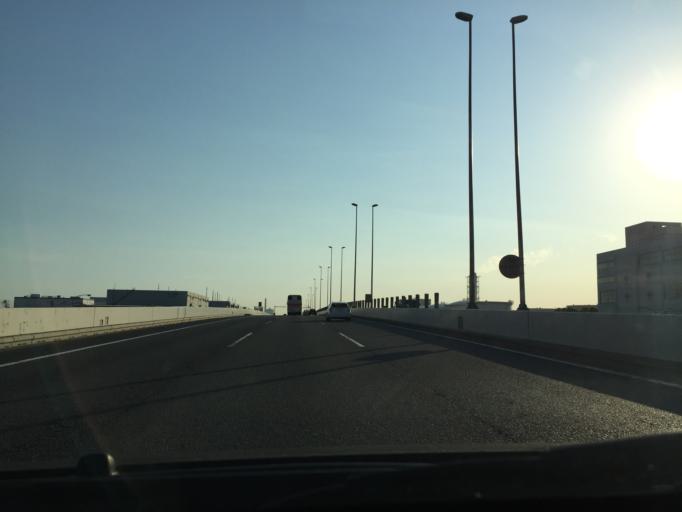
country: JP
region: Kanagawa
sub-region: Kawasaki-shi
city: Kawasaki
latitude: 35.4989
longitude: 139.7601
